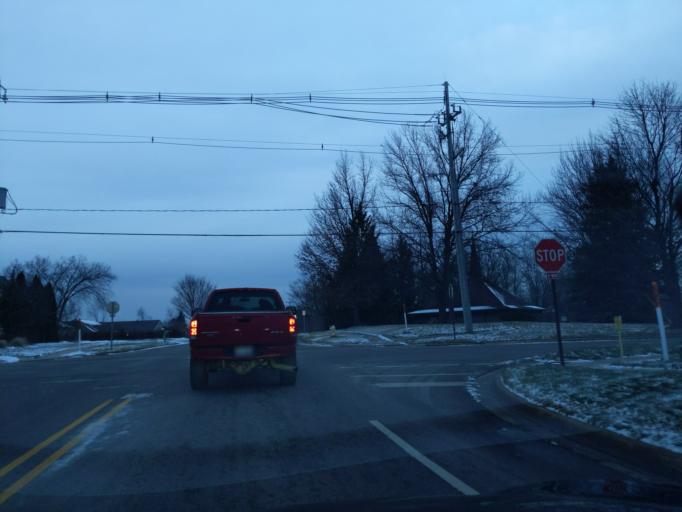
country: US
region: Michigan
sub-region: Ingham County
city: Mason
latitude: 42.5748
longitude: -84.4528
